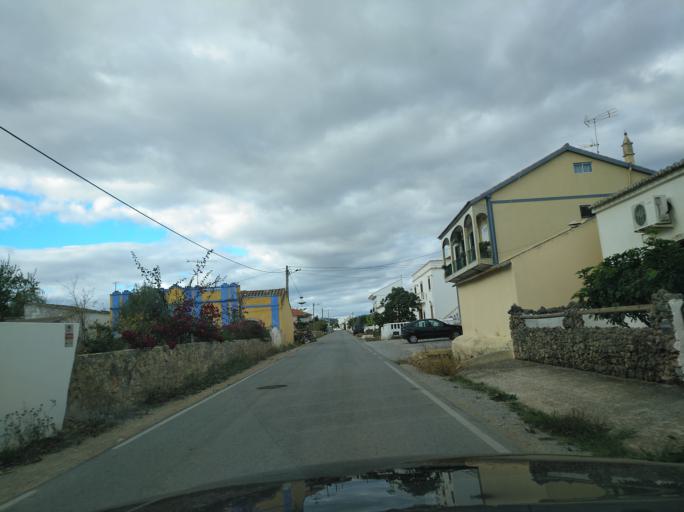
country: PT
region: Faro
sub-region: Tavira
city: Luz
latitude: 37.0989
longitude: -7.7070
